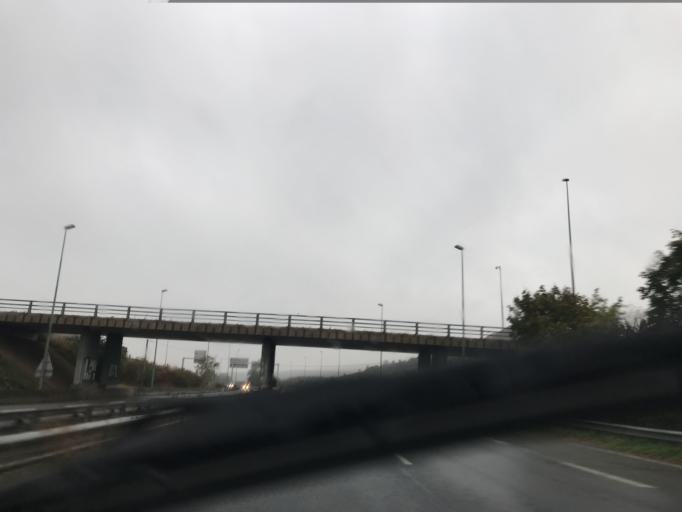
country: FR
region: Auvergne
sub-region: Departement du Puy-de-Dome
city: Aubiere
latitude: 45.7776
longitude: 3.1297
